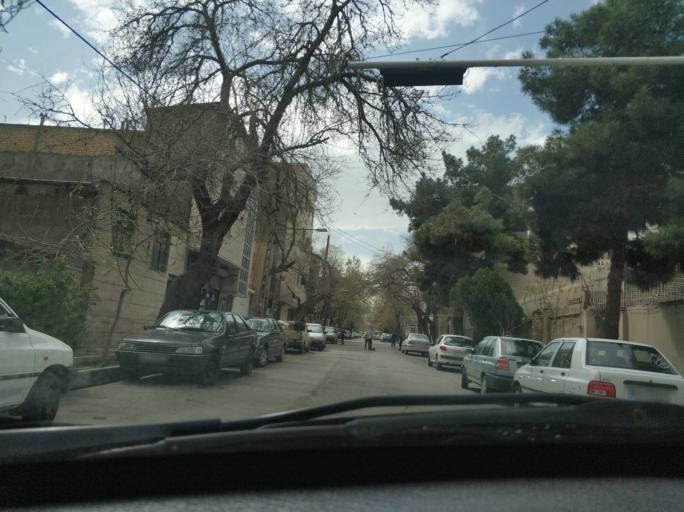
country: IR
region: Razavi Khorasan
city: Mashhad
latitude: 36.2793
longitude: 59.5741
